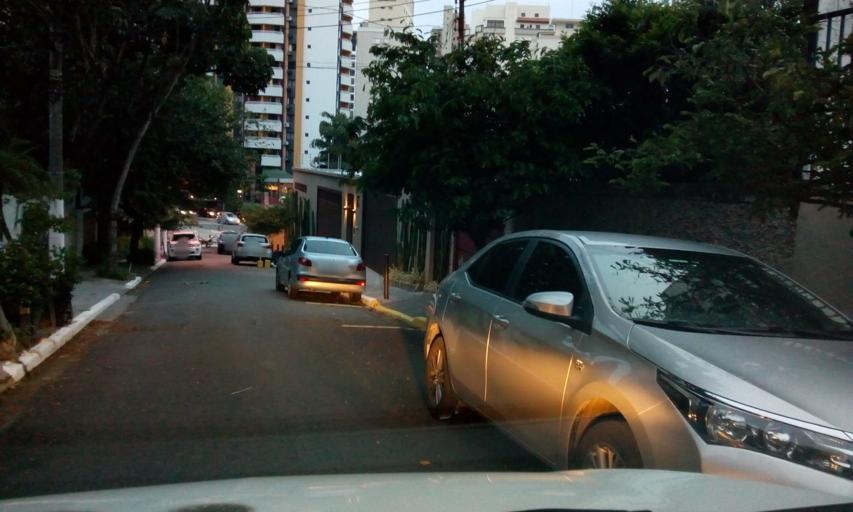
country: BR
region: Sao Paulo
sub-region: Sao Paulo
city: Sao Paulo
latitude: -23.5967
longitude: -46.6666
